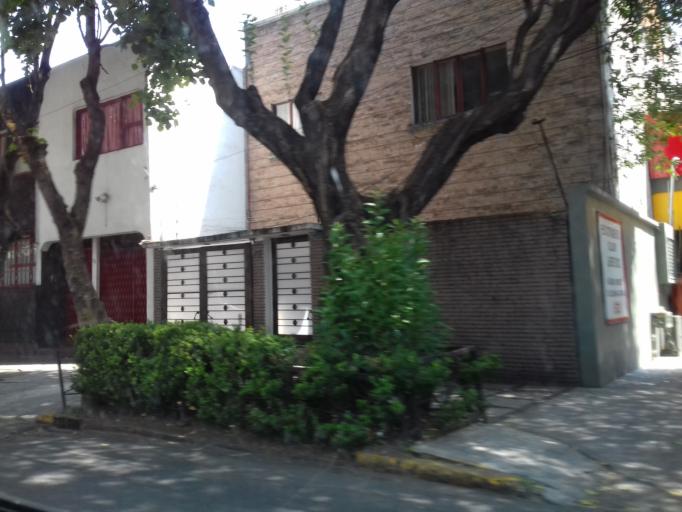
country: MX
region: Mexico City
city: Benito Juarez
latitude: 19.3989
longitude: -99.1613
